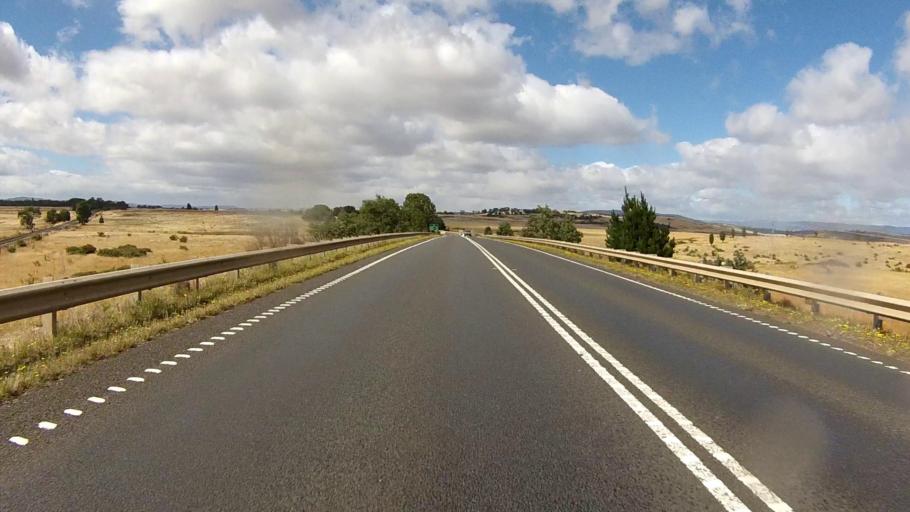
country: AU
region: Tasmania
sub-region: Northern Midlands
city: Evandale
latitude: -41.8399
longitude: 147.4482
